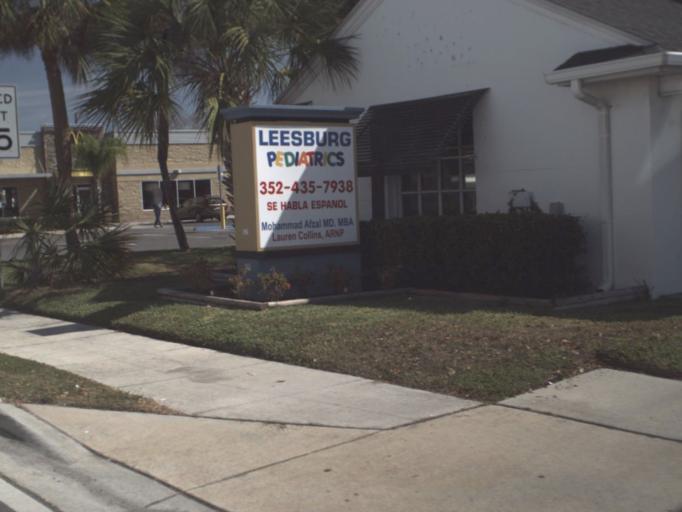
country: US
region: Florida
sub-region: Lake County
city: Leesburg
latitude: 28.8238
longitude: -81.8874
